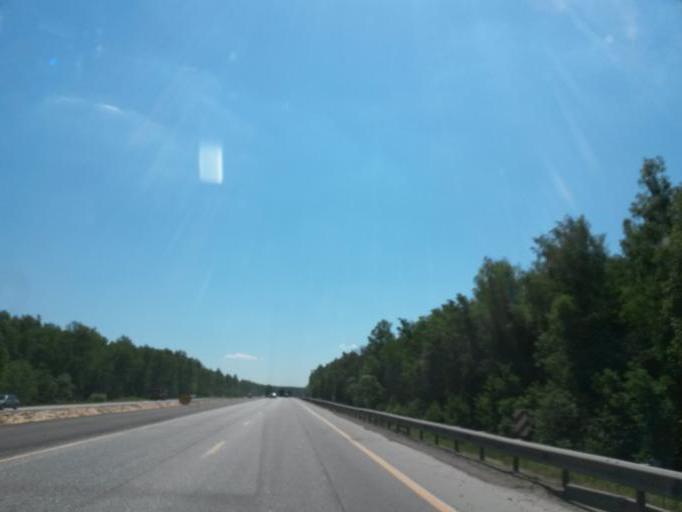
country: RU
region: Moskovskaya
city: Novyy Byt
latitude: 55.1188
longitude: 37.5746
